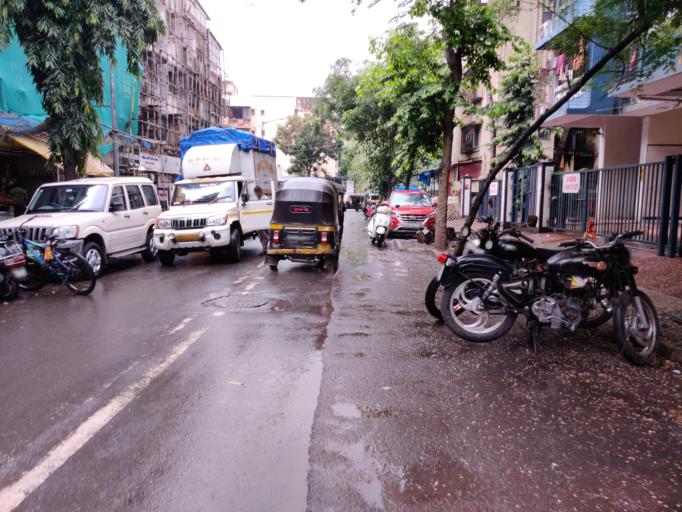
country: IN
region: Maharashtra
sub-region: Mumbai Suburban
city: Borivli
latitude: 19.2559
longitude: 72.8595
